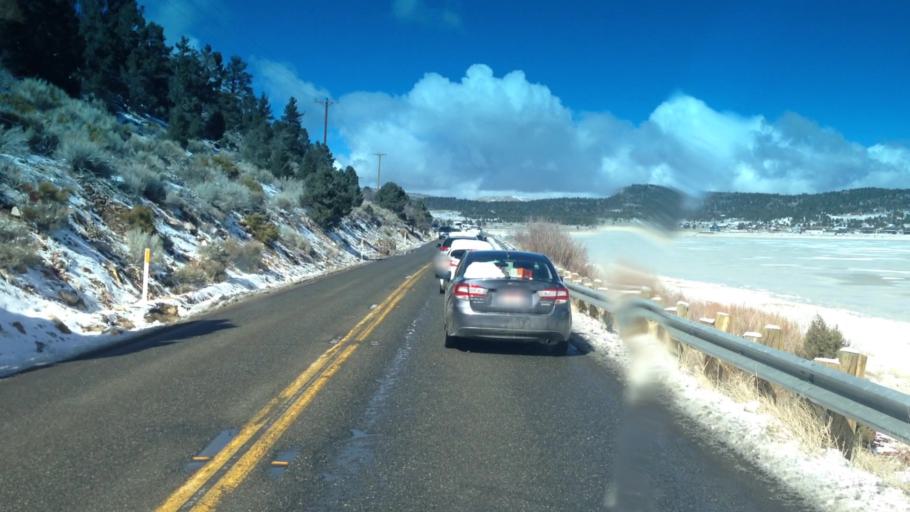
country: US
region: California
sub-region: San Bernardino County
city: Big Bear City
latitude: 34.2786
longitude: -116.8142
